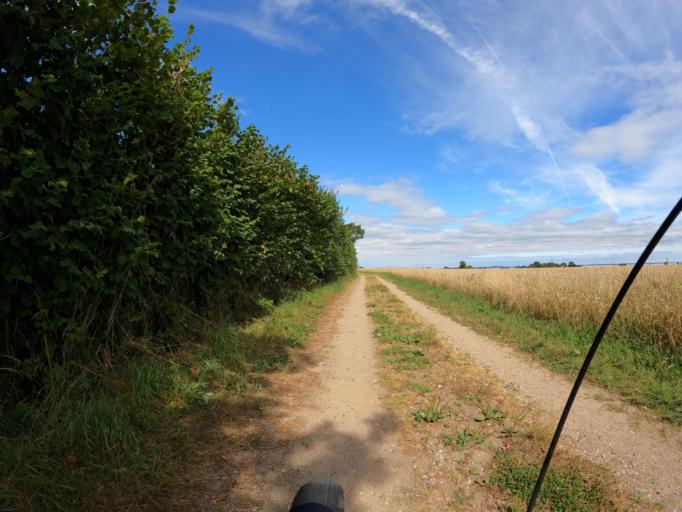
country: DE
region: Schleswig-Holstein
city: Steinbergkirche
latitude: 54.7863
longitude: 9.7547
